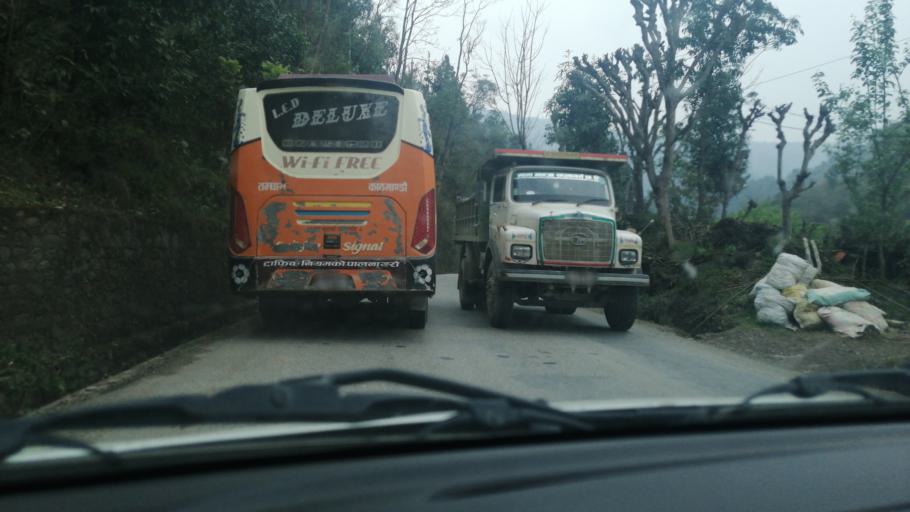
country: NP
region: Western Region
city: Tansen
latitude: 27.8111
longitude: 83.5229
